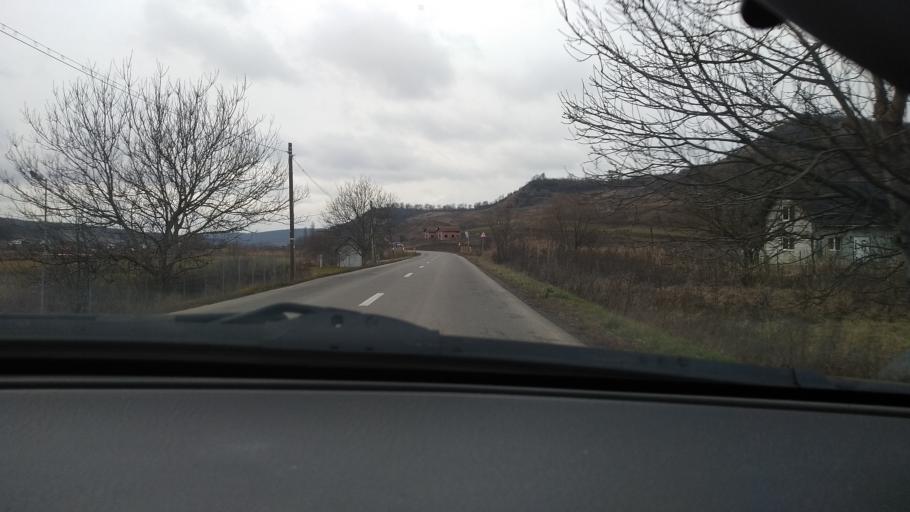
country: RO
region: Mures
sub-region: Comuna Livezeni
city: Livezeni
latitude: 46.5434
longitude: 24.6685
